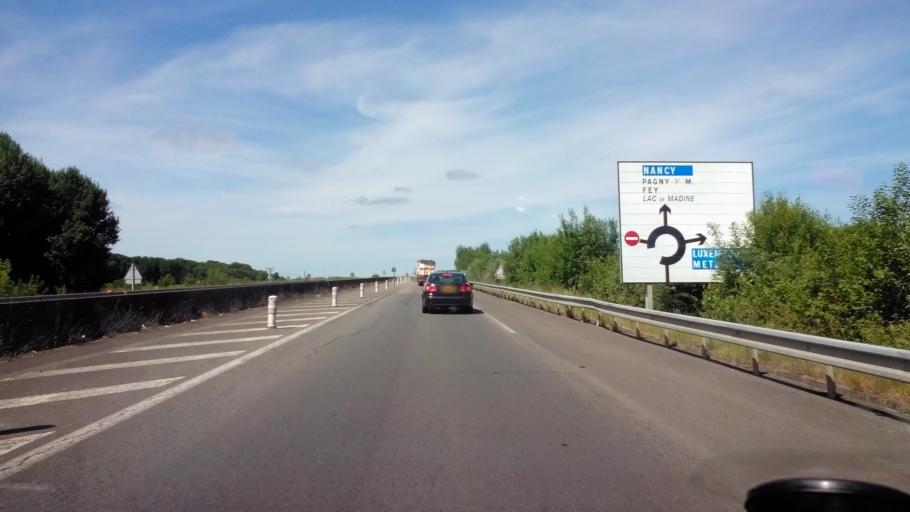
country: FR
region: Lorraine
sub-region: Departement de la Moselle
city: Augny
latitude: 49.0371
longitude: 6.1174
